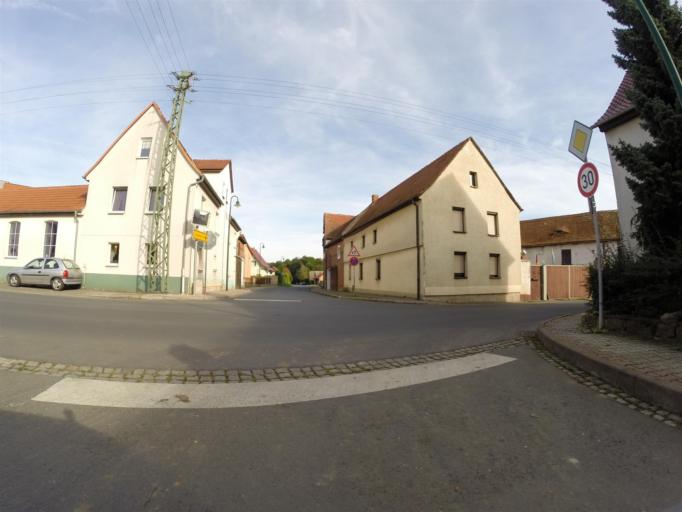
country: DE
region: Thuringia
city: Grossschwabhausen
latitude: 50.9616
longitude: 11.5225
